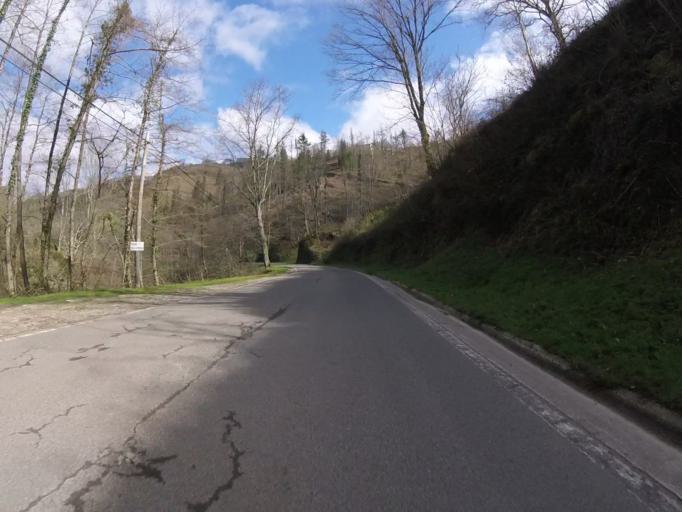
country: ES
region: Navarre
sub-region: Provincia de Navarra
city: Goizueta
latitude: 43.1575
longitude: -1.8498
